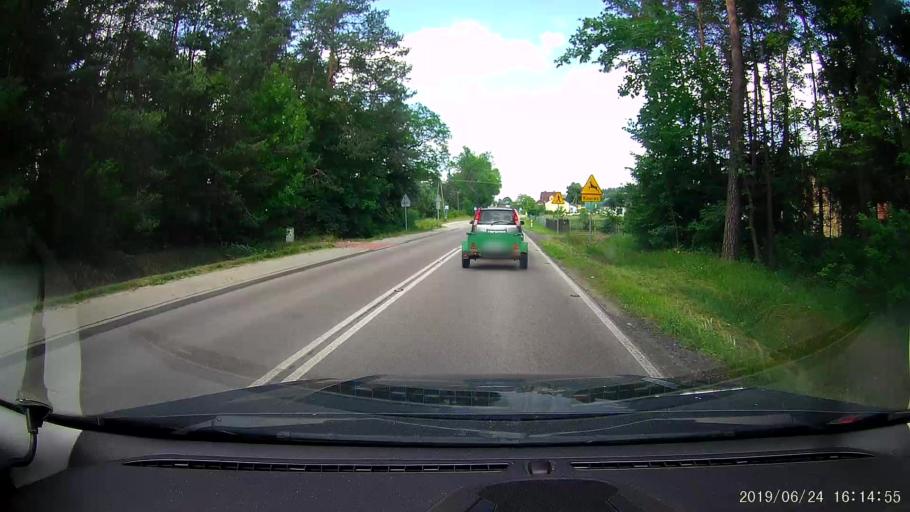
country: PL
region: Lublin Voivodeship
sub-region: Powiat tomaszowski
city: Belzec
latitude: 50.3775
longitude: 23.3925
